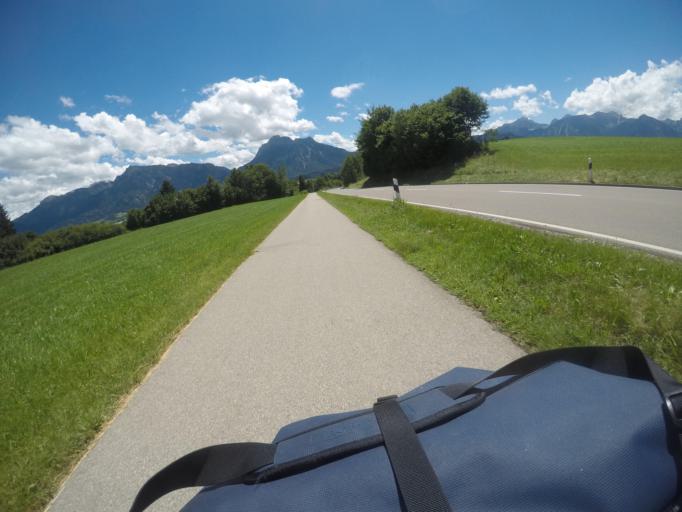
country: DE
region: Bavaria
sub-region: Swabia
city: Fuessen
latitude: 47.6005
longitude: 10.7094
